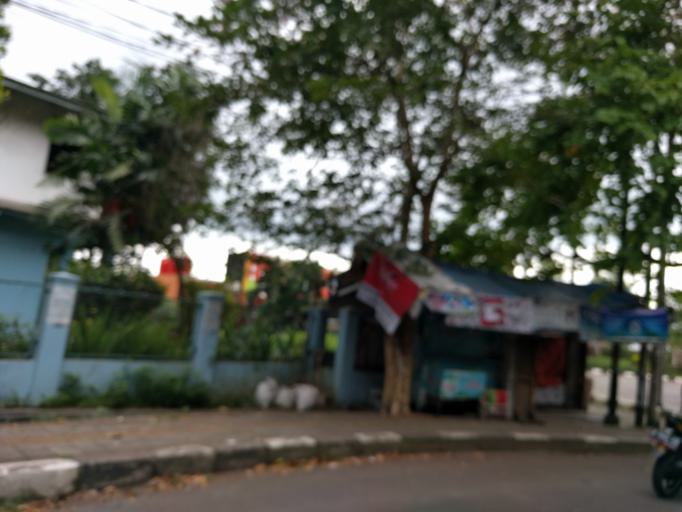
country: ID
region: West Java
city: Bogor
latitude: -6.5913
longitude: 106.8082
